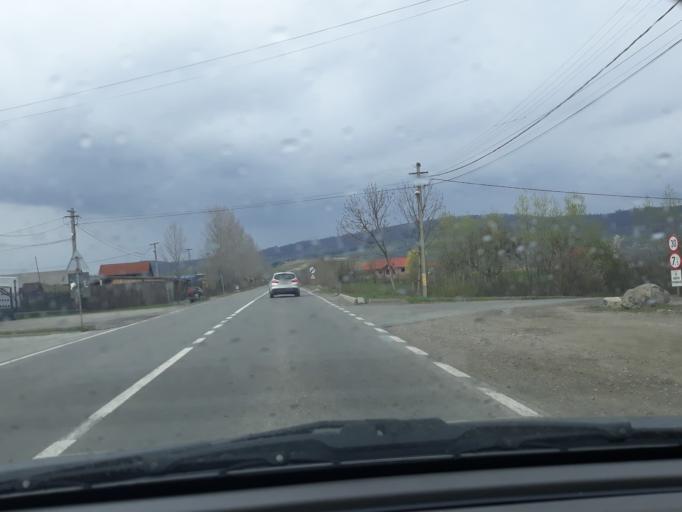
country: RO
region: Harghita
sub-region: Comuna Lupeni
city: Lupeni
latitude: 46.3838
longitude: 25.2184
